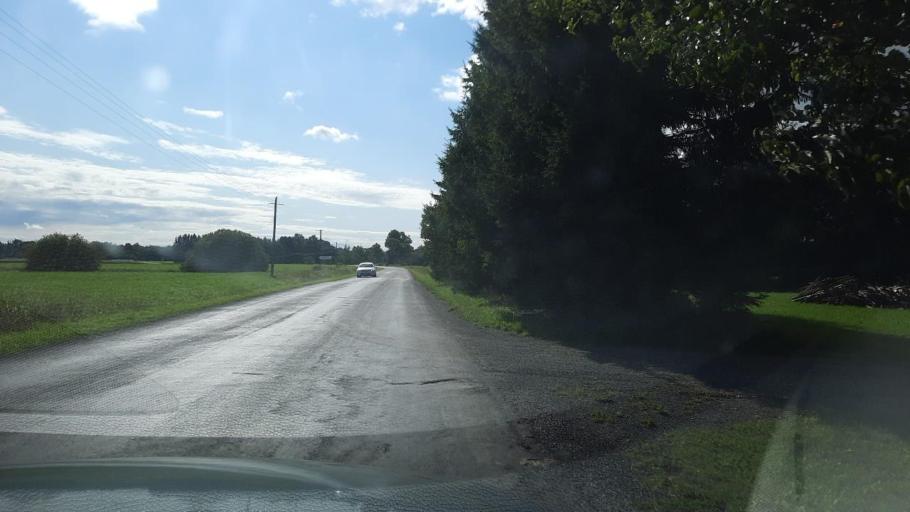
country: EE
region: Paernumaa
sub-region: Tootsi vald
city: Tootsi
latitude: 58.4885
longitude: 24.9288
